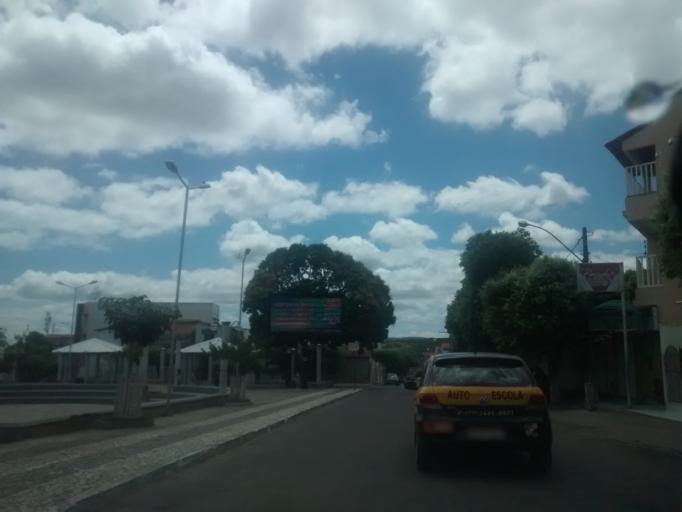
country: BR
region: Bahia
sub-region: Brumado
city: Brumado
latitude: -14.2047
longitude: -41.6712
